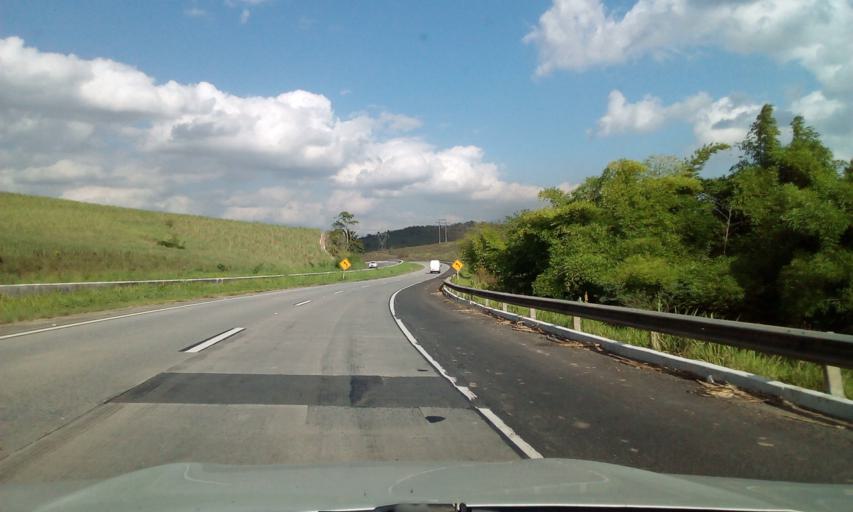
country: BR
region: Pernambuco
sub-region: Joaquim Nabuco
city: Joaquim Nabuco
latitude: -8.6032
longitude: -35.5363
